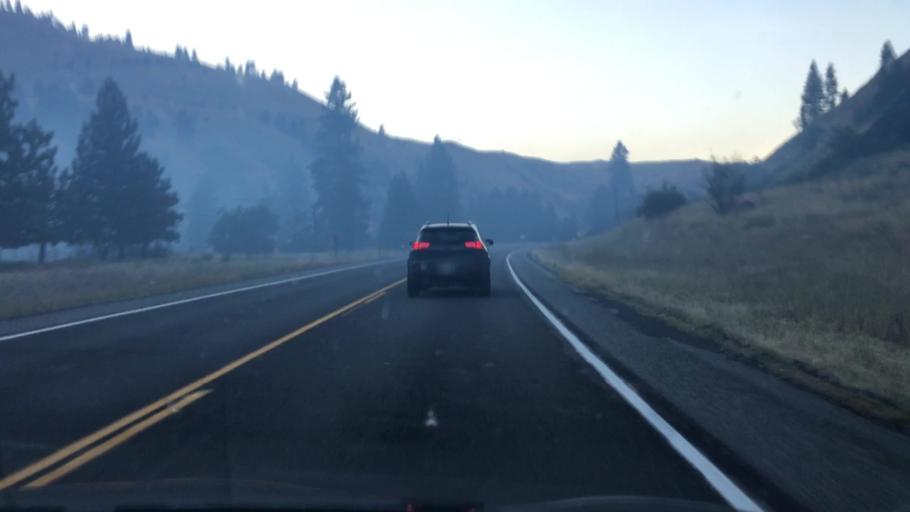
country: US
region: Idaho
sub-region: Valley County
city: McCall
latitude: 45.2883
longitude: -116.3549
